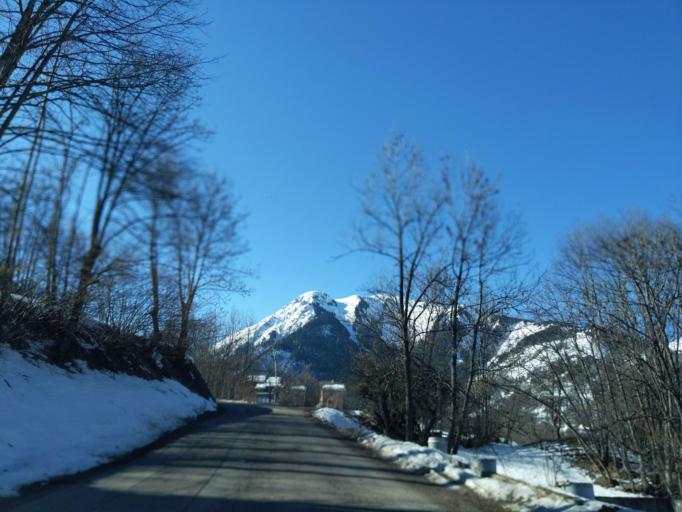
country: FR
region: Rhone-Alpes
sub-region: Departement de la Savoie
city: Saint-Martin-de-Belleville
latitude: 45.4220
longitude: 6.4970
